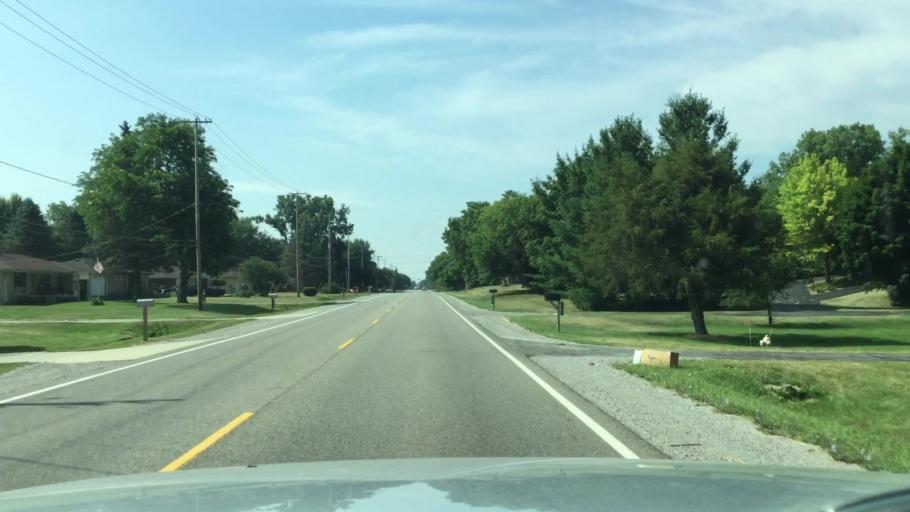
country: US
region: Michigan
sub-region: Genesee County
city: Flushing
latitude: 43.0722
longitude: -83.8134
